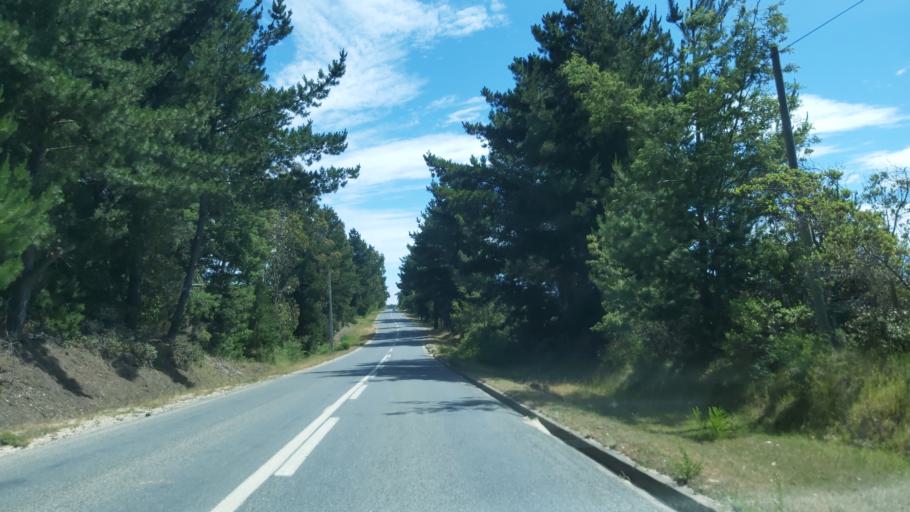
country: CL
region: Maule
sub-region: Provincia de Talca
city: Constitucion
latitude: -35.5600
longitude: -72.5877
